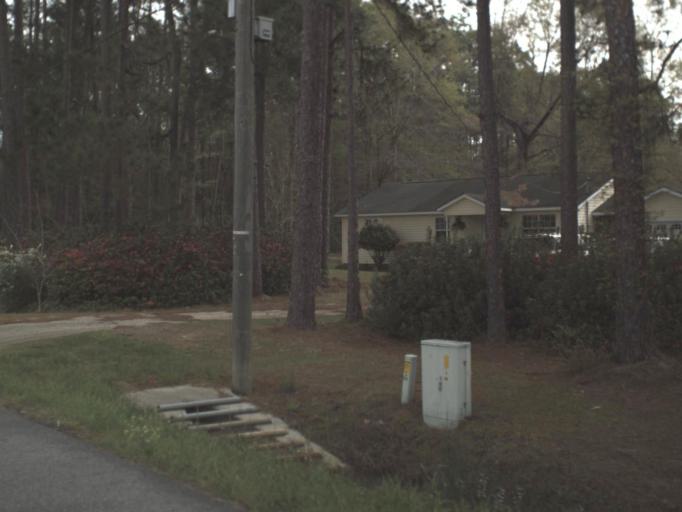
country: US
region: Florida
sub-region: Holmes County
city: Bonifay
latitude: 30.8130
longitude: -85.6736
